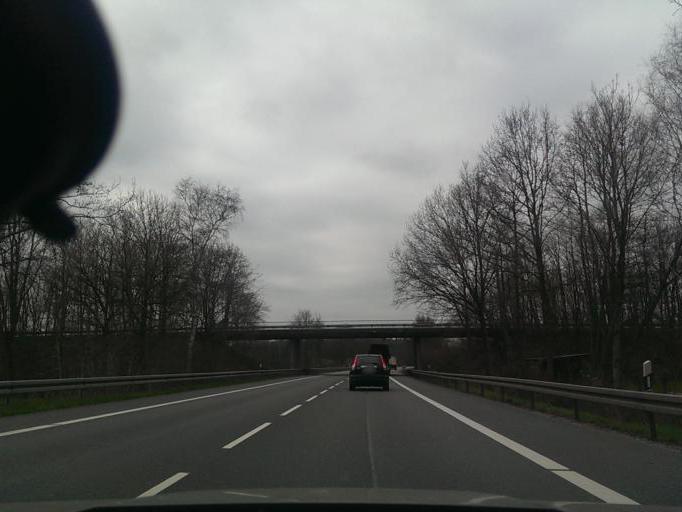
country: DE
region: North Rhine-Westphalia
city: Rietberg
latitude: 51.7954
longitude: 8.4169
